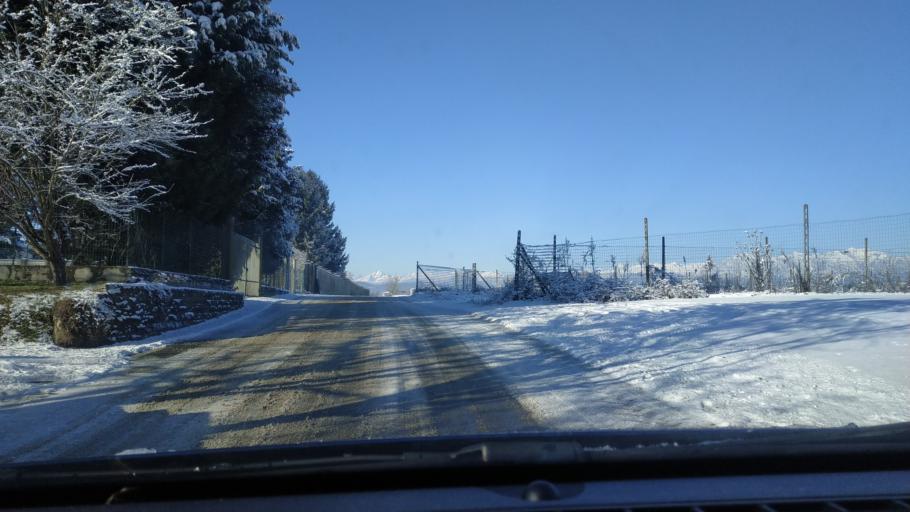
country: IT
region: Piedmont
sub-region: Provincia di Torino
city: Vische
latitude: 45.3372
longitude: 7.9486
